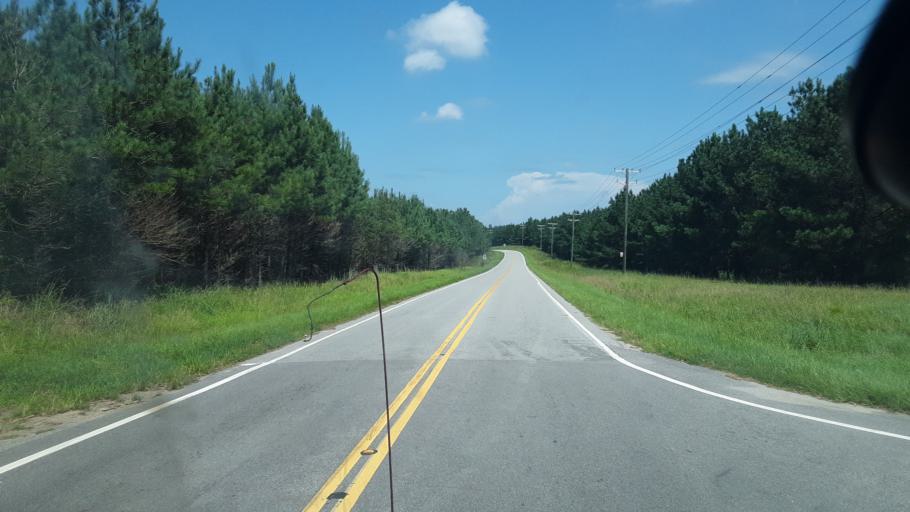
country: US
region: South Carolina
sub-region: Bamberg County
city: Bamberg
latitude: 33.4083
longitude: -81.0164
